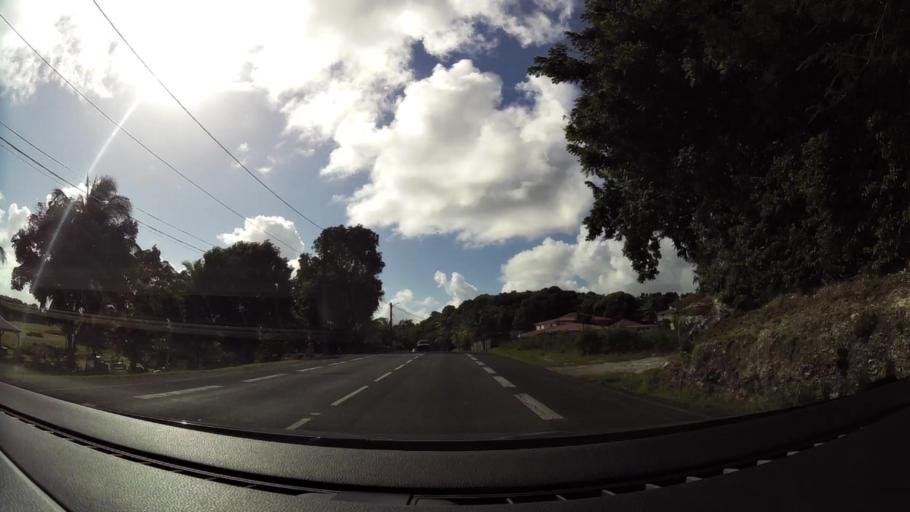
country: GP
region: Guadeloupe
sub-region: Guadeloupe
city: Le Gosier
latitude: 16.2081
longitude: -61.4514
